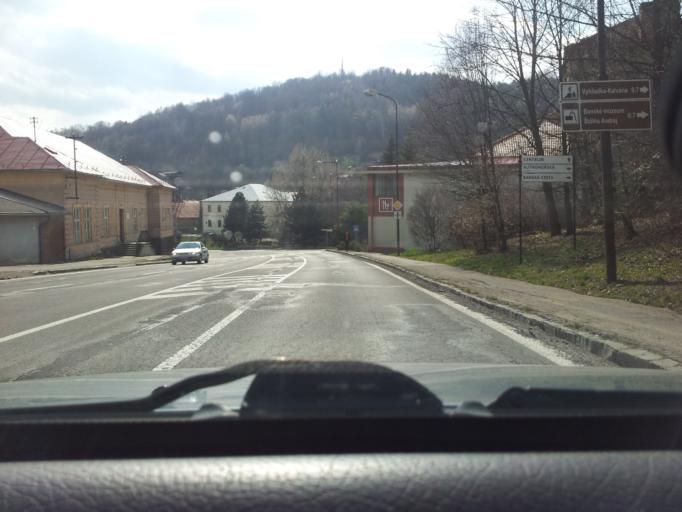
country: SK
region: Banskobystricky
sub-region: Okres Ziar nad Hronom
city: Kremnica
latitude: 48.7089
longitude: 18.9157
